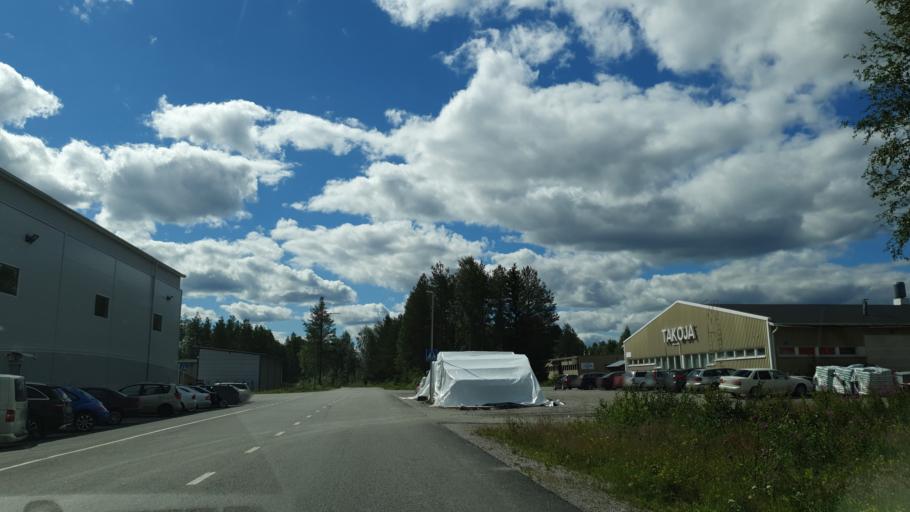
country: FI
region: Kainuu
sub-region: Kehys-Kainuu
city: Kuhmo
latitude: 64.1332
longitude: 29.4728
